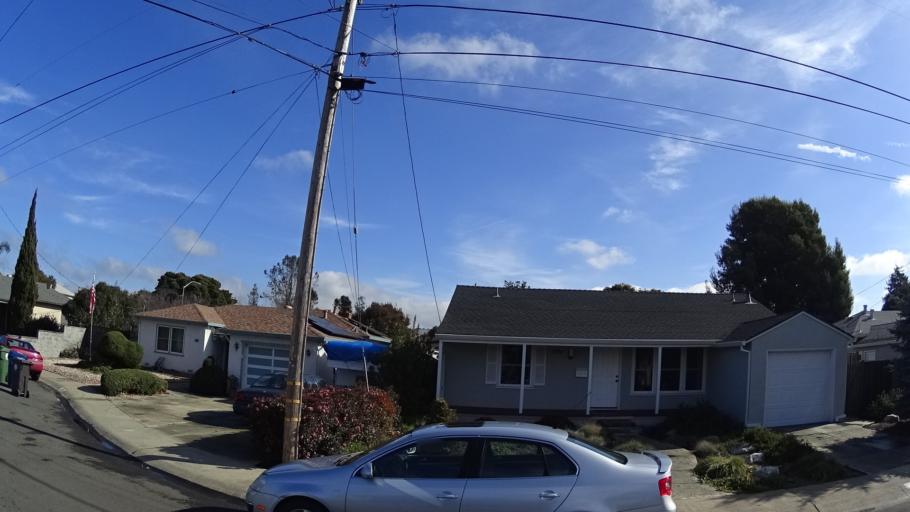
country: US
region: California
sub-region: Alameda County
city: Castro Valley
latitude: 37.6886
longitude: -122.0746
